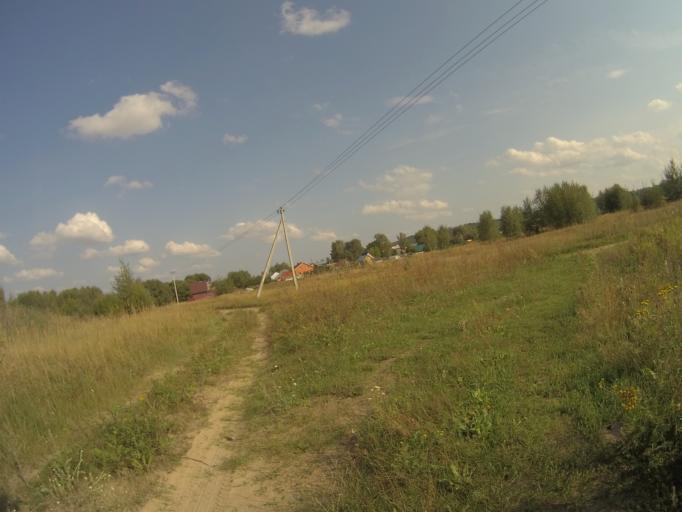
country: RU
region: Vladimir
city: Raduzhnyy
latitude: 56.0283
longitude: 40.3103
